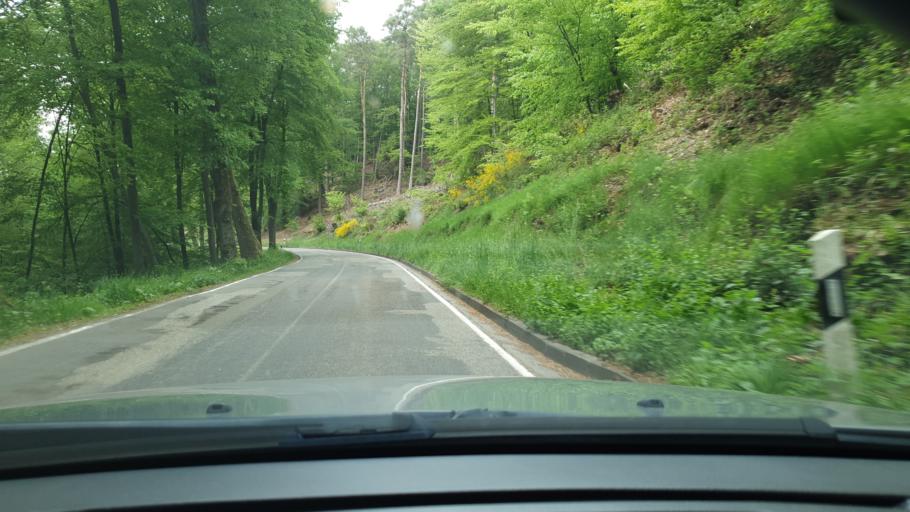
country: DE
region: Rheinland-Pfalz
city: Martinshohe
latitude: 49.3766
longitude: 7.4844
